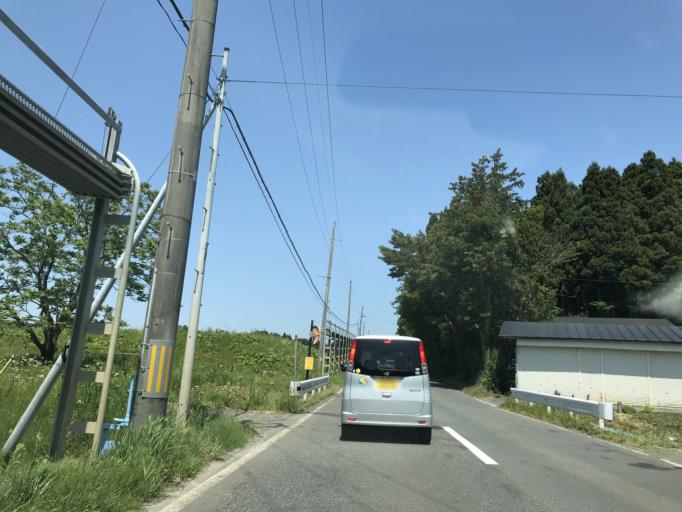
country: JP
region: Iwate
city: Kitakami
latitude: 39.2635
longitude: 141.0617
